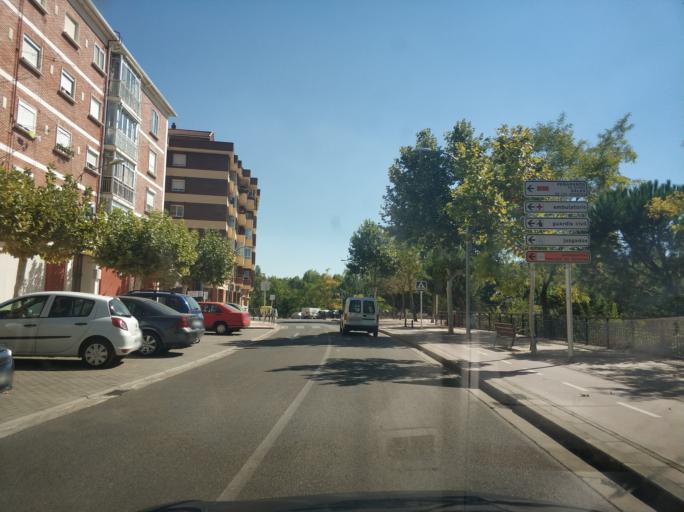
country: ES
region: Castille and Leon
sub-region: Provincia de Burgos
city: Aranda de Duero
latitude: 41.6689
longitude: -3.6798
